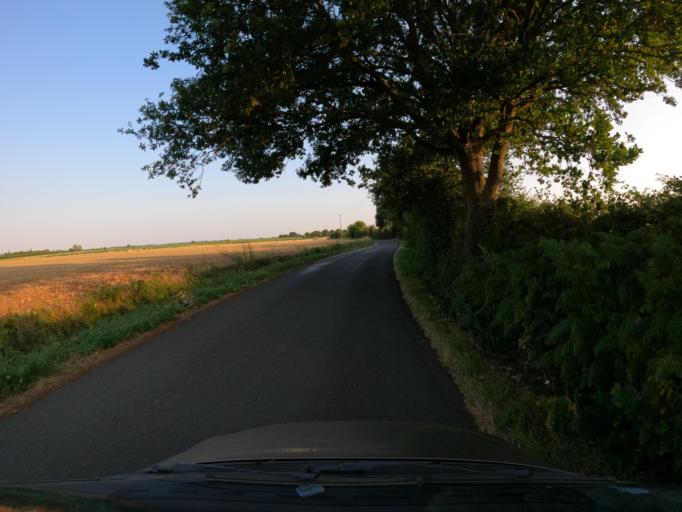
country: FR
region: Pays de la Loire
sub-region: Departement de la Sarthe
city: Parce-sur-Sarthe
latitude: 47.8974
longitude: -0.2186
